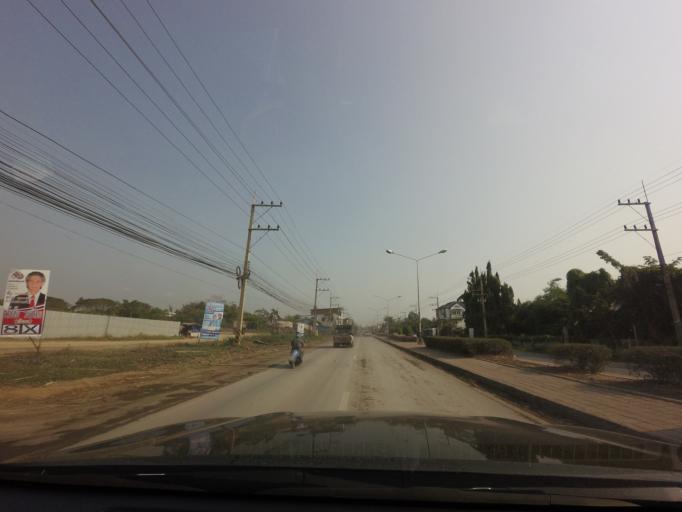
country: TH
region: Kanchanaburi
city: Tha Maka
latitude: 13.8902
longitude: 99.7988
